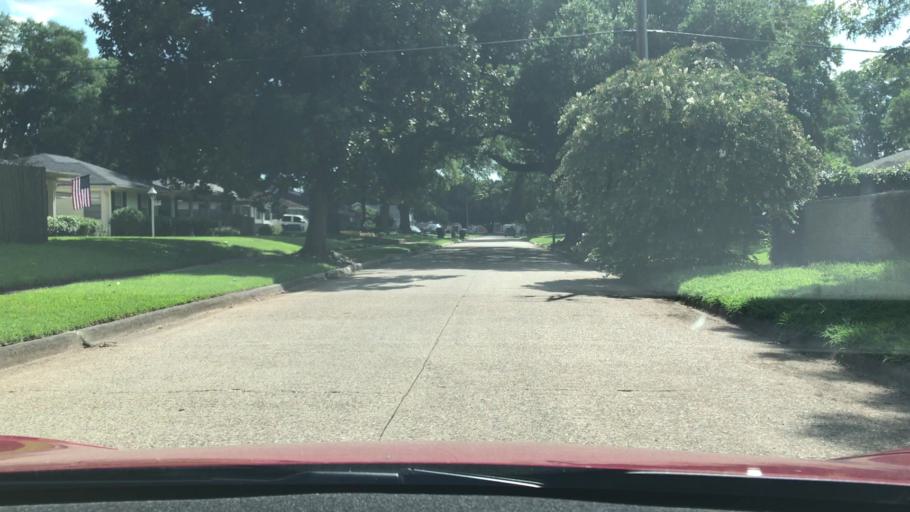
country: US
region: Louisiana
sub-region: Bossier Parish
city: Bossier City
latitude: 32.4611
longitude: -93.7134
